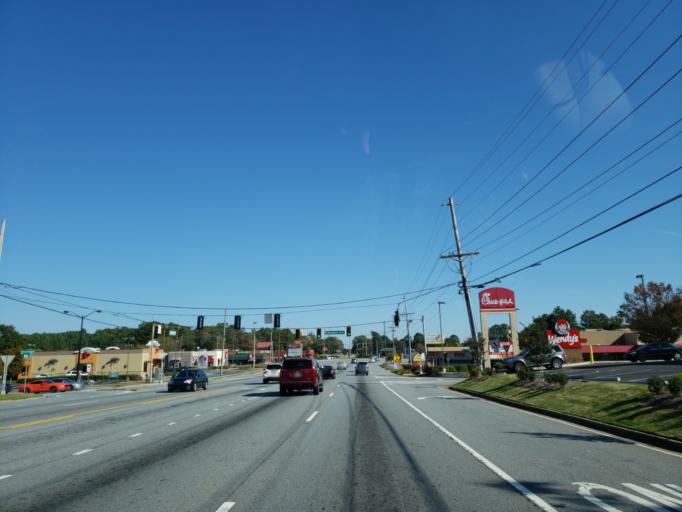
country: US
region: Georgia
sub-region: Gwinnett County
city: Lawrenceville
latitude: 33.9662
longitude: -84.0118
